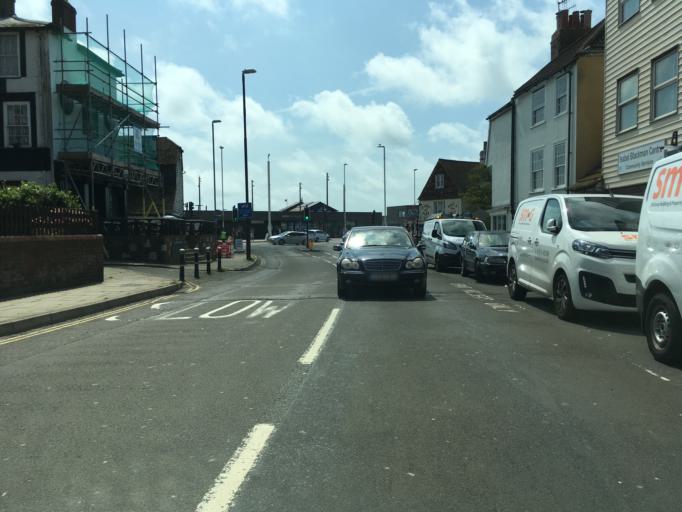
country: GB
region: England
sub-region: East Sussex
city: Hastings
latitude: 50.8568
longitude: 0.5923
